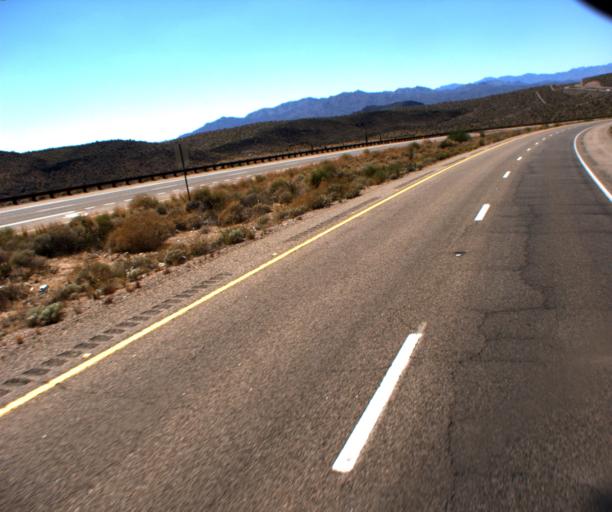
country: US
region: Arizona
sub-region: Yavapai County
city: Bagdad
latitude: 34.5724
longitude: -113.4865
